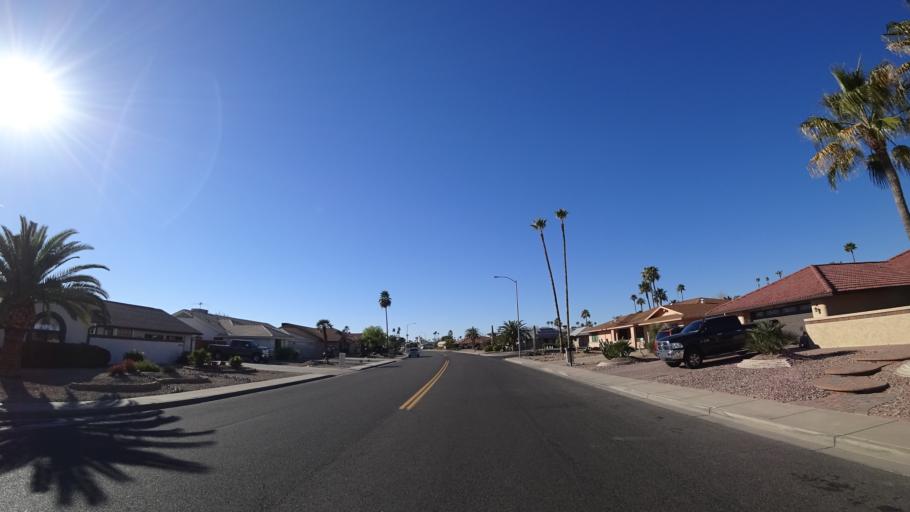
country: US
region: Arizona
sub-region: Maricopa County
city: Sun City West
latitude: 33.6718
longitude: -112.3457
